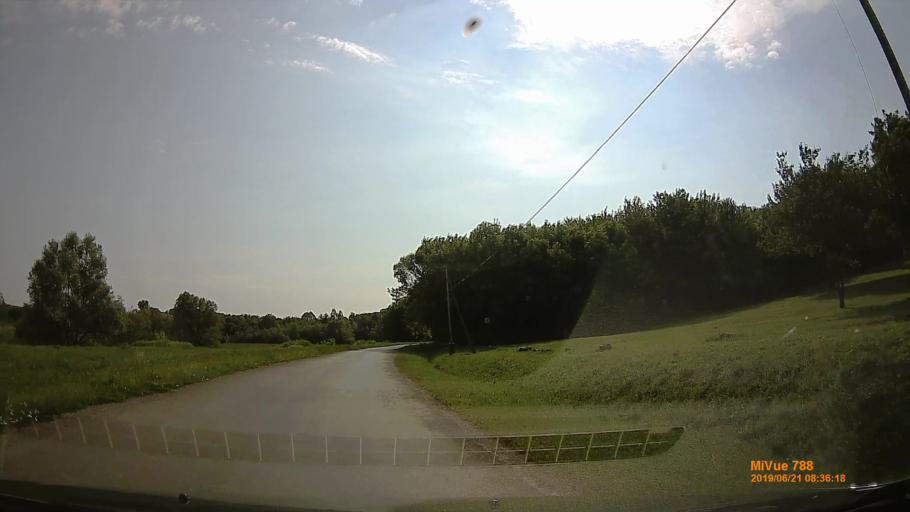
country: HU
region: Baranya
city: Buekkoesd
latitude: 46.1725
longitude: 17.9050
